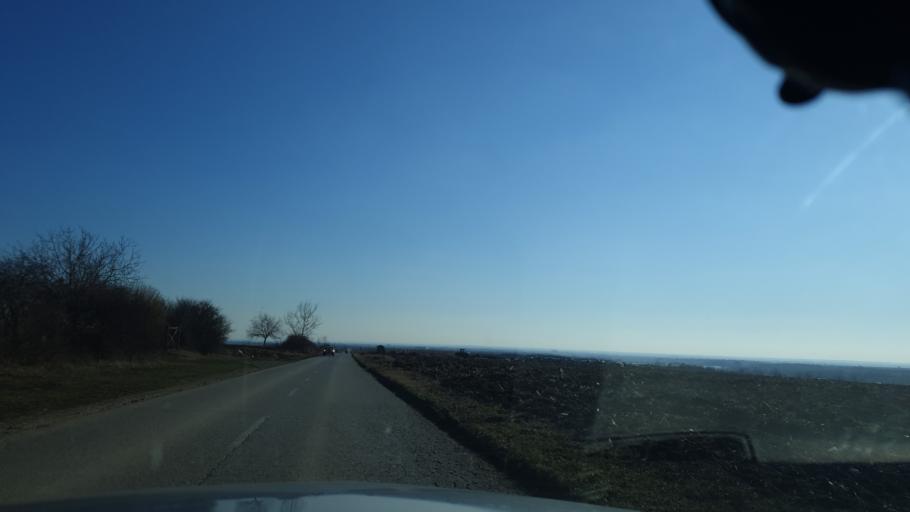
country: RS
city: Vrdnik
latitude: 45.0906
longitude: 19.8060
